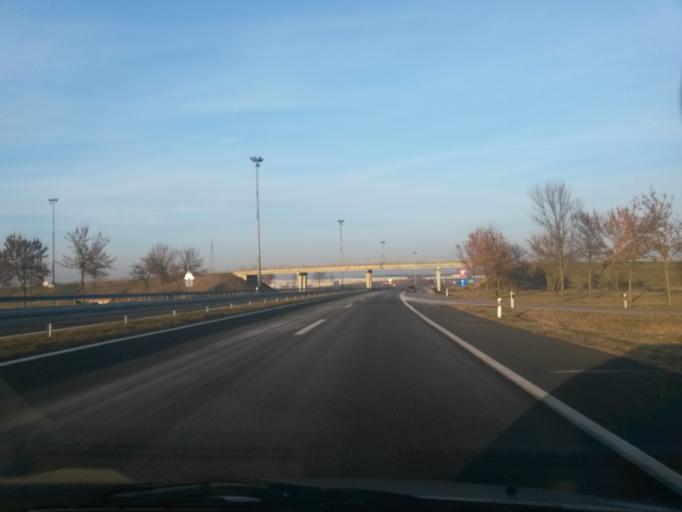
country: HR
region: Medimurska
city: Kursanec
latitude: 46.2598
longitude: 16.3999
